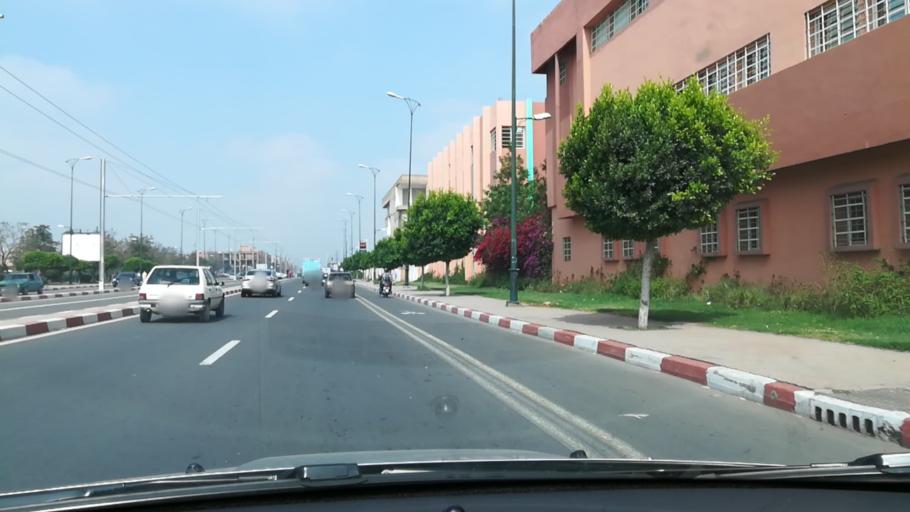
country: MA
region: Marrakech-Tensift-Al Haouz
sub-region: Marrakech
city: Marrakesh
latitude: 31.6278
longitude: -8.0553
